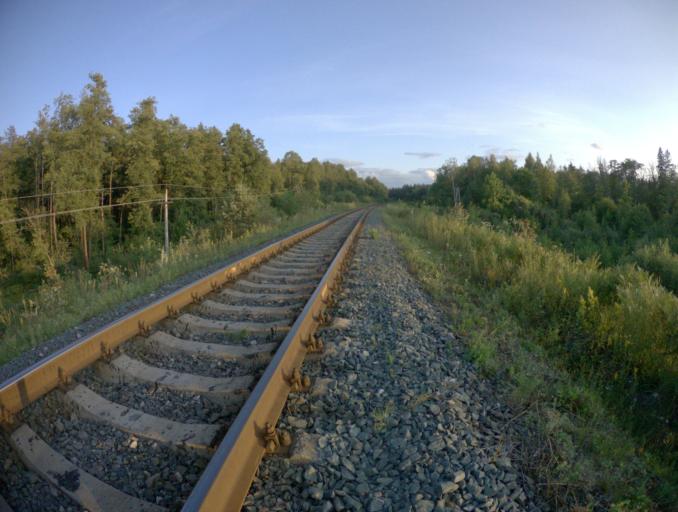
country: RU
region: Vladimir
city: Raduzhnyy
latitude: 56.0382
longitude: 40.3842
